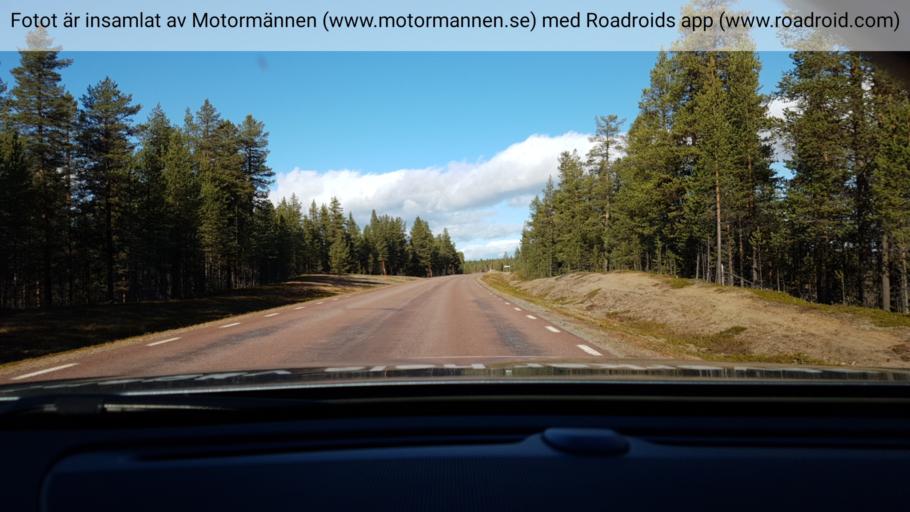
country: SE
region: Norrbotten
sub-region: Arjeplogs Kommun
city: Arjeplog
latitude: 66.0269
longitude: 18.0642
